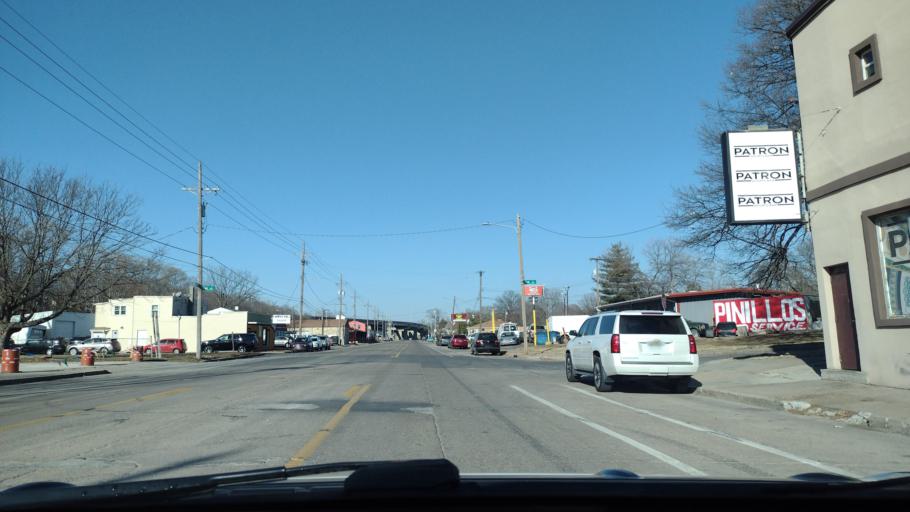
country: US
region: Nebraska
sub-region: Douglas County
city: Omaha
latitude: 41.1917
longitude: -95.9374
